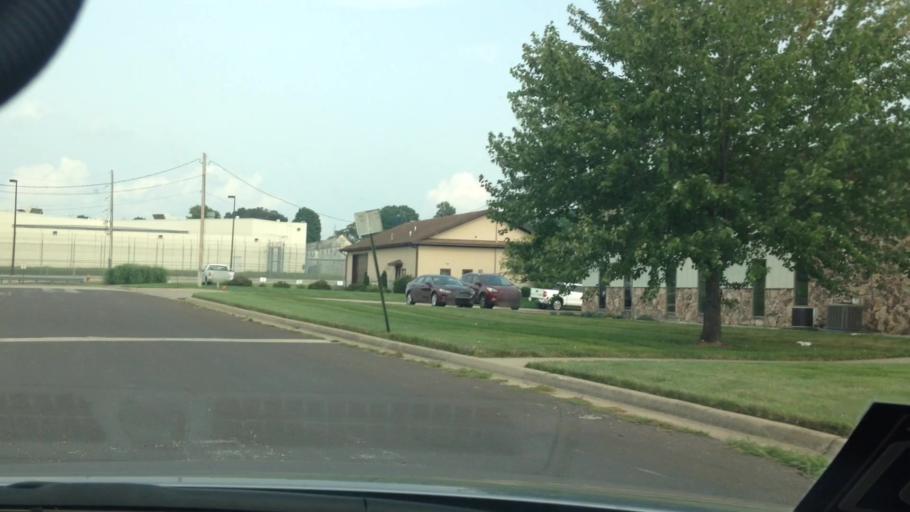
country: US
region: Kansas
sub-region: Leavenworth County
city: Lansing
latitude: 39.2732
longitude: -94.8944
